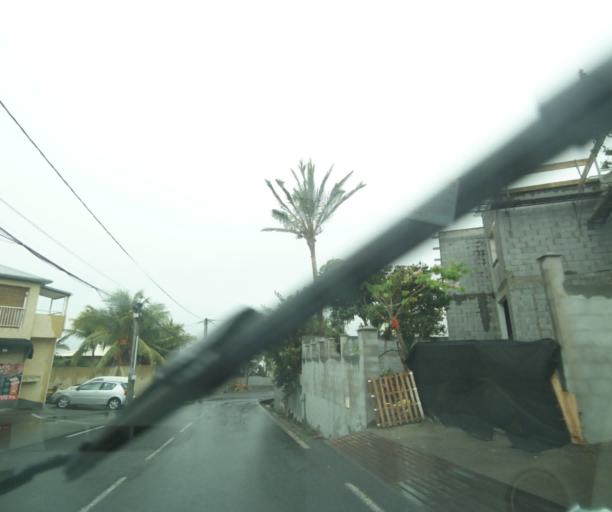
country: RE
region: Reunion
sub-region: Reunion
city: Saint-Paul
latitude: -21.0212
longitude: 55.2882
